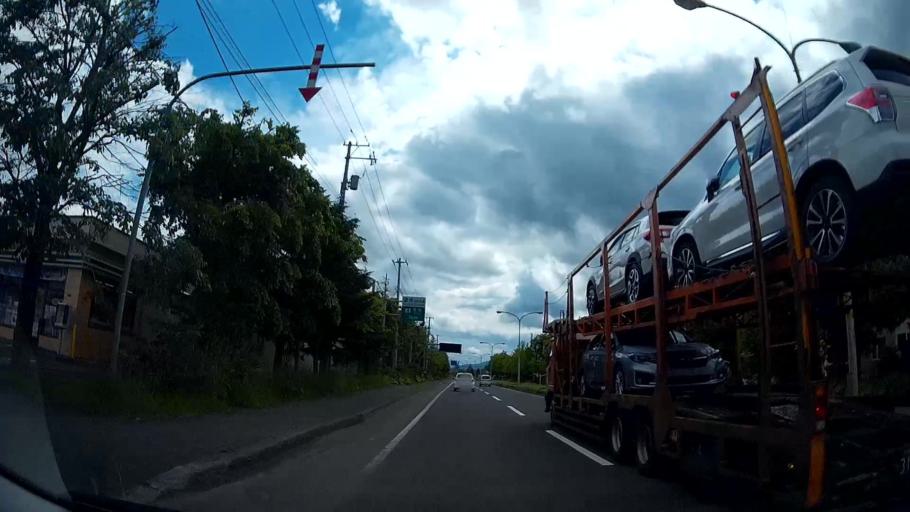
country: JP
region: Hokkaido
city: Kitahiroshima
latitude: 42.8776
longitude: 141.5673
